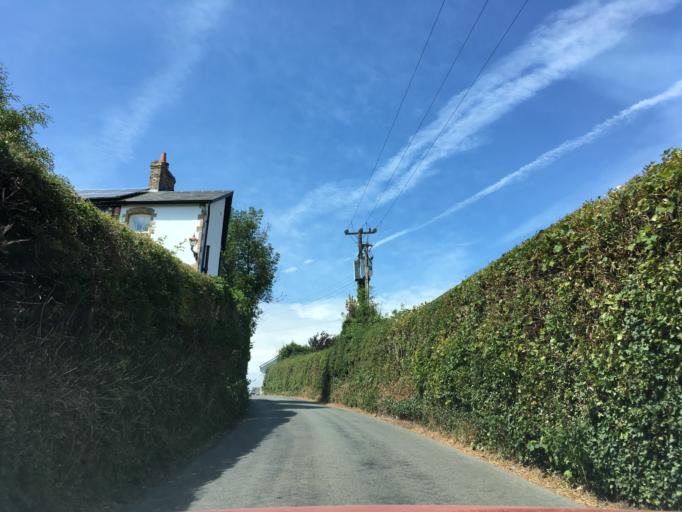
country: GB
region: Wales
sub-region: Caerphilly County Borough
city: Machen
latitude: 51.5722
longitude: -3.1526
